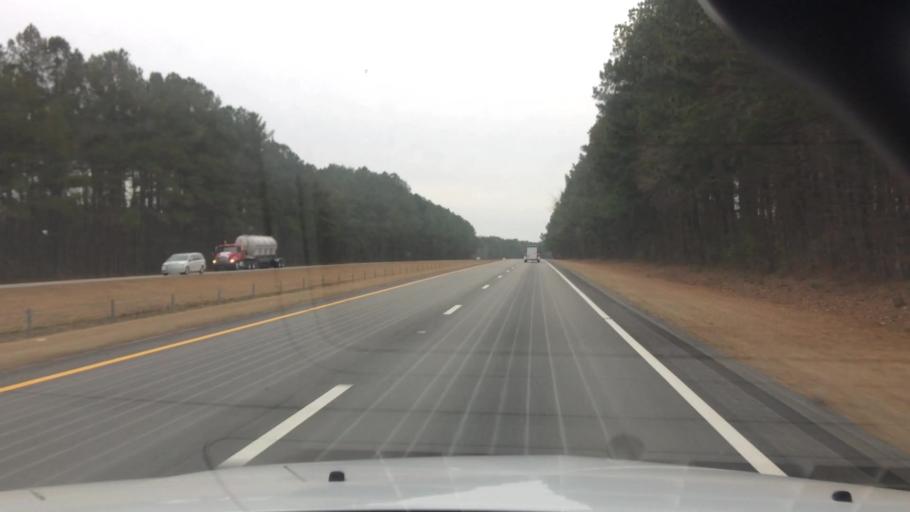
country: US
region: North Carolina
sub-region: Nash County
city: Spring Hope
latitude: 35.8999
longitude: -78.1854
